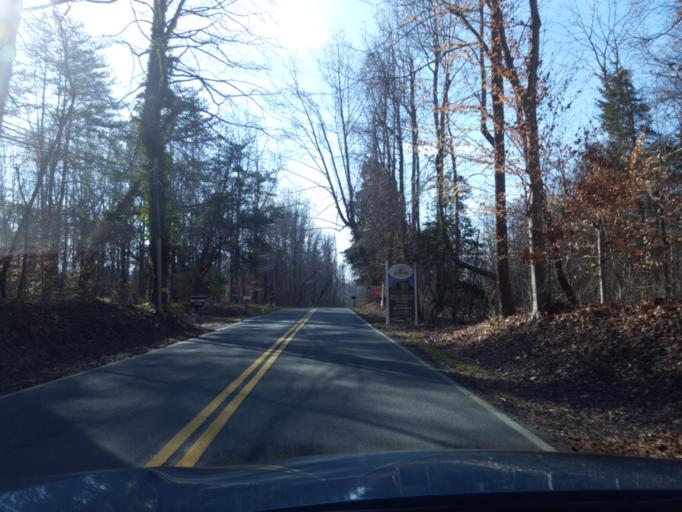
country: US
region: Maryland
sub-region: Calvert County
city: Chesapeake Beach
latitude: 38.6242
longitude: -76.5324
